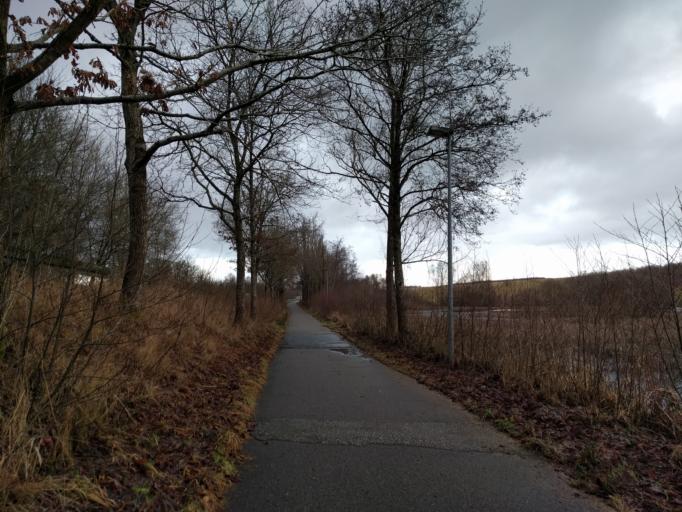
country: DK
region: Central Jutland
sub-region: Viborg Kommune
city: Viborg
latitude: 56.4404
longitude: 9.4270
